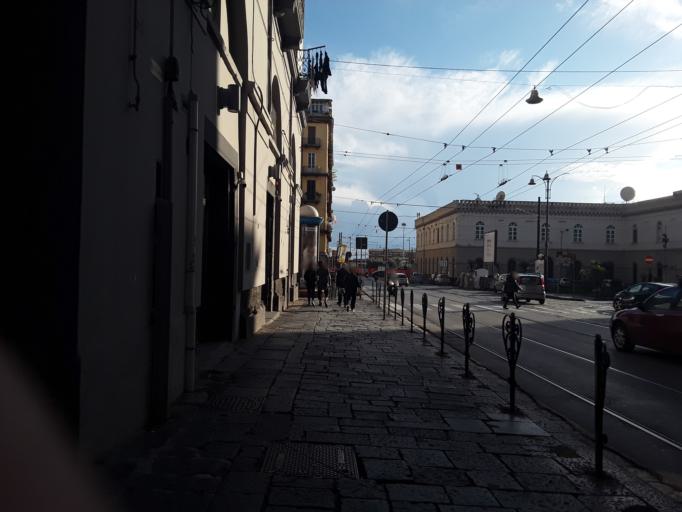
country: IT
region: Campania
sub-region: Provincia di Napoli
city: Napoli
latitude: 40.8477
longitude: 14.2690
